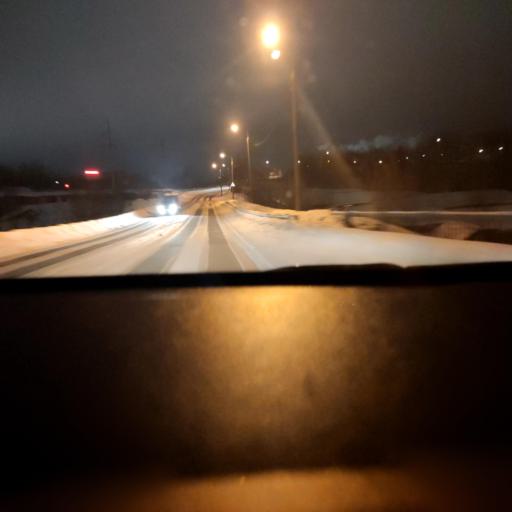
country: RU
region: Tatarstan
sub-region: Chistopol'skiy Rayon
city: Chistopol'
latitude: 55.3593
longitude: 50.6136
